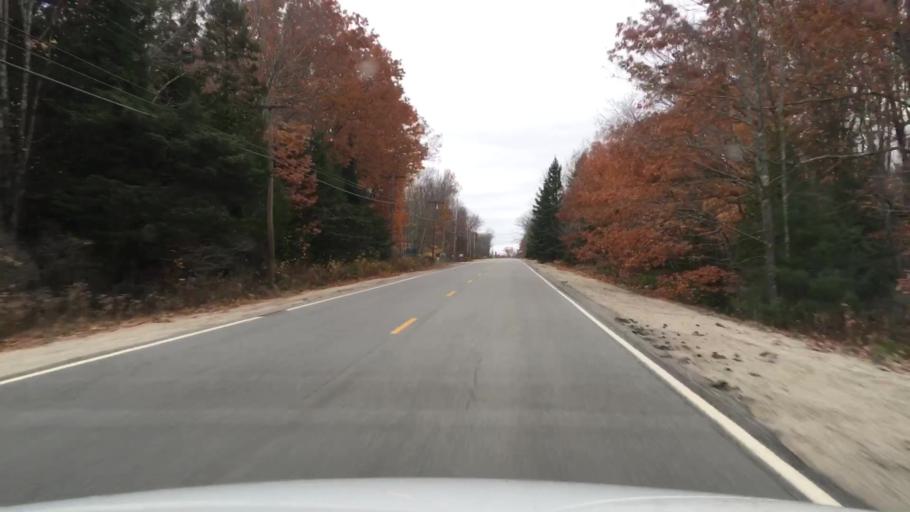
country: US
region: Maine
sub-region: Hancock County
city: Sedgwick
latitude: 44.3976
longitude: -68.5880
